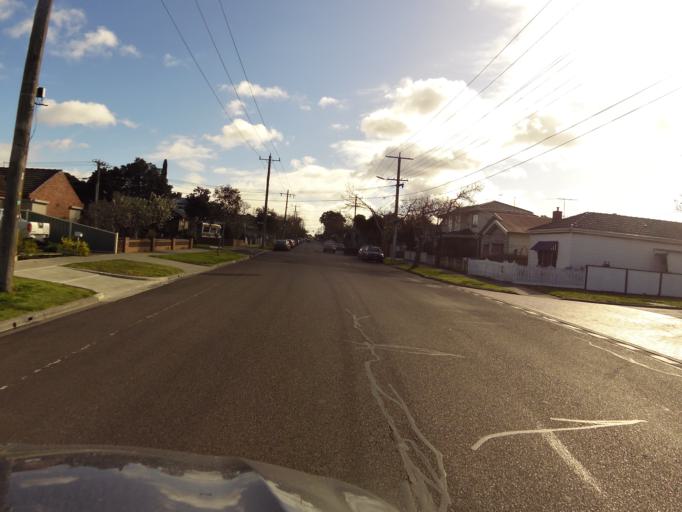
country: AU
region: Victoria
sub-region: Maribyrnong
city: Kingsville
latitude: -37.8074
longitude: 144.8704
